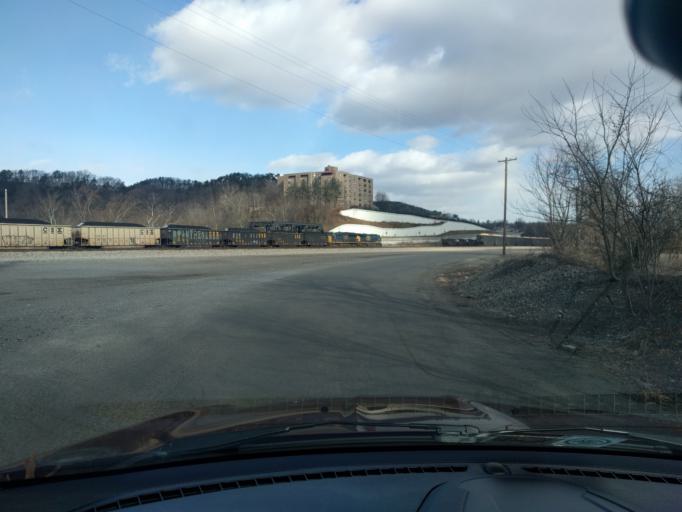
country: US
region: Virginia
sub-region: Alleghany County
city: Clifton Forge
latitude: 37.8082
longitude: -79.8443
